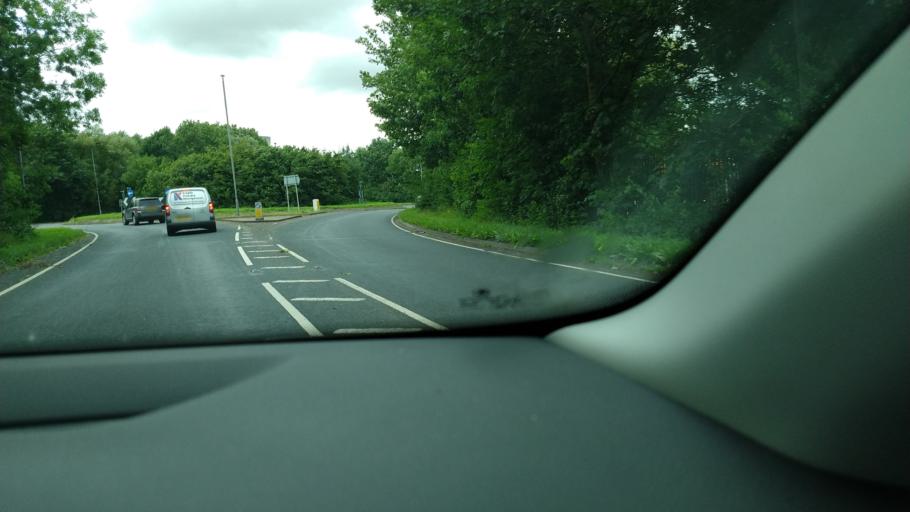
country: GB
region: England
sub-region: North Yorkshire
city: Camblesforth
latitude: 53.7290
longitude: -0.9923
